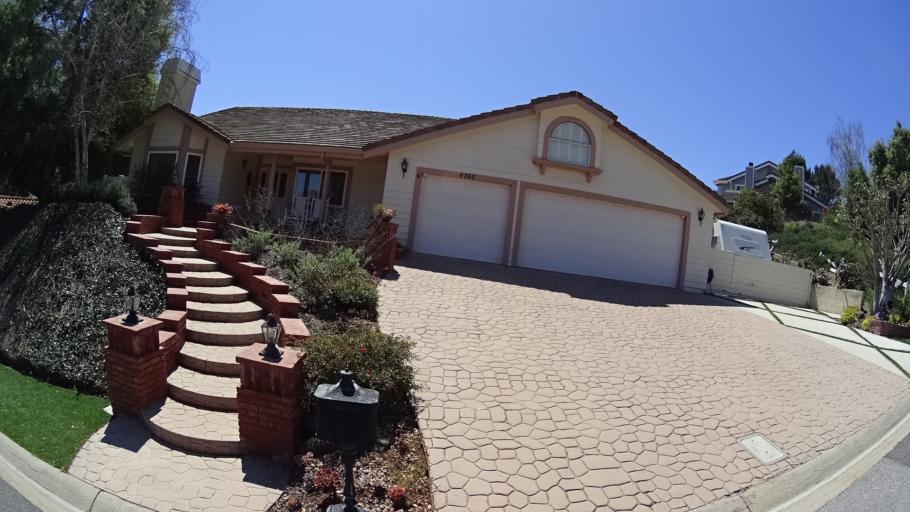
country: US
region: California
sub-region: Ventura County
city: Casa Conejo
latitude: 34.1630
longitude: -118.9634
